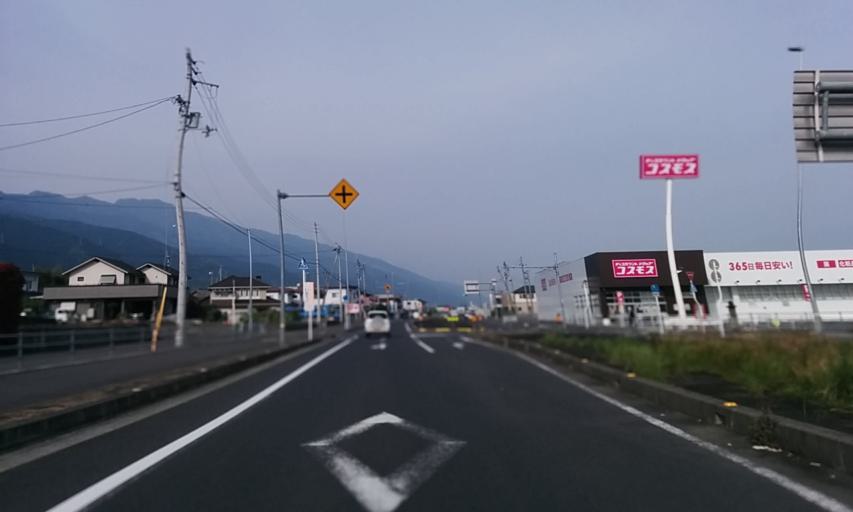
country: JP
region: Ehime
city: Kawanoecho
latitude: 33.9738
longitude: 133.5411
